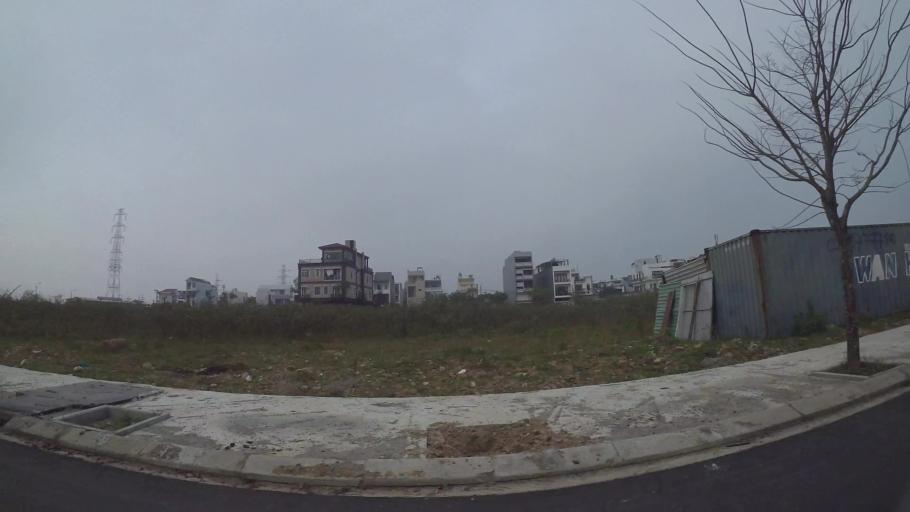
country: VN
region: Da Nang
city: Ngu Hanh Son
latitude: 16.0188
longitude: 108.2342
